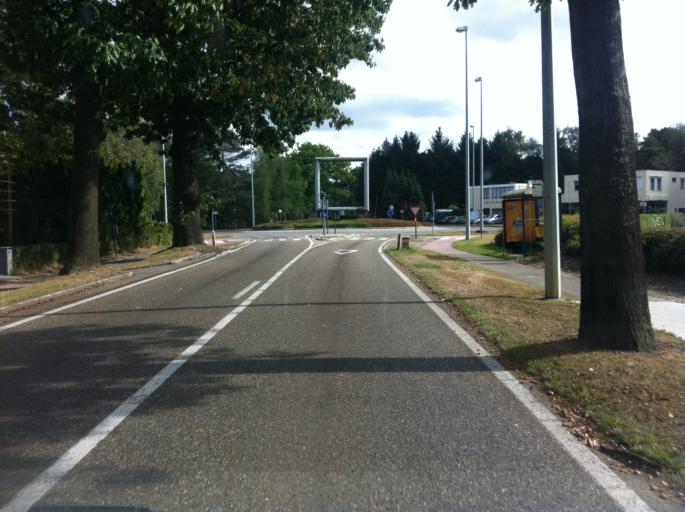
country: BE
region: Flanders
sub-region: Provincie Limburg
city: Maasmechelen
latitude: 50.9746
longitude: 5.6722
